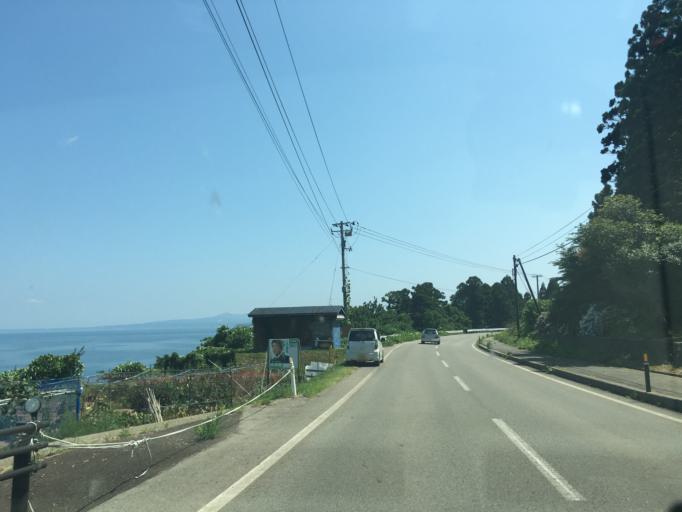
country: JP
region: Akita
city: Tenno
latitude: 39.9962
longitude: 139.7105
